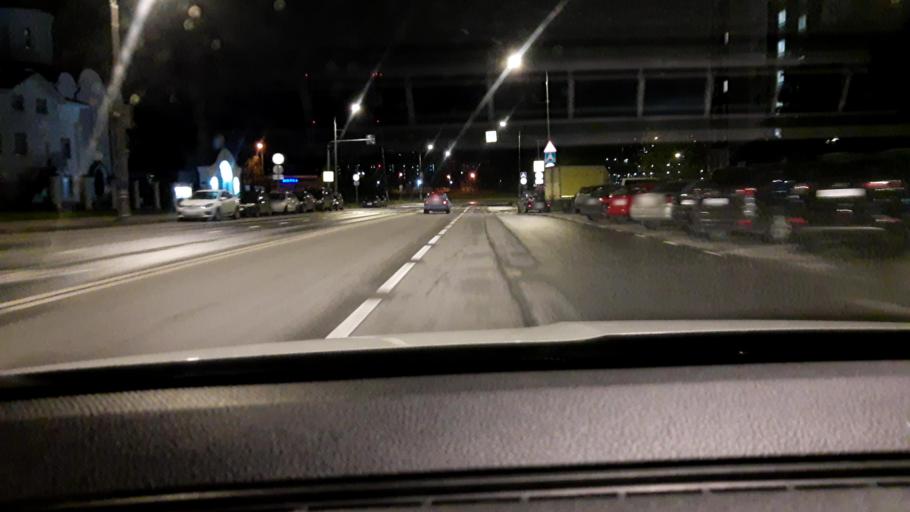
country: RU
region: Moskovskaya
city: Andreyevka
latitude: 55.9899
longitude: 37.1526
